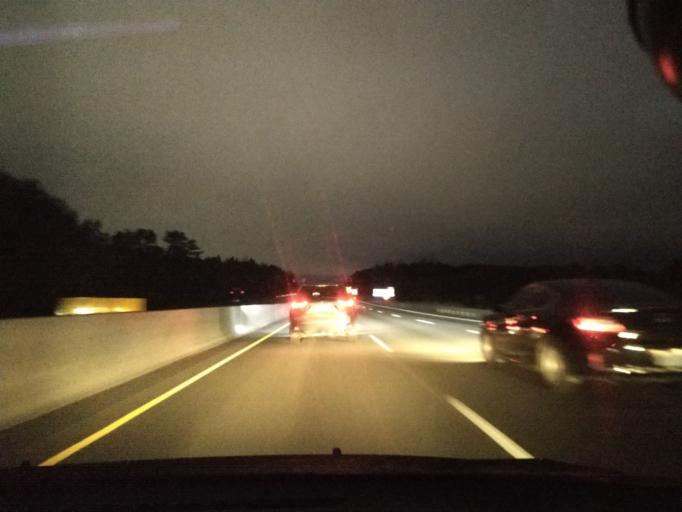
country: CA
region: Ontario
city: Innisfil
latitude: 44.3187
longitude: -79.6830
